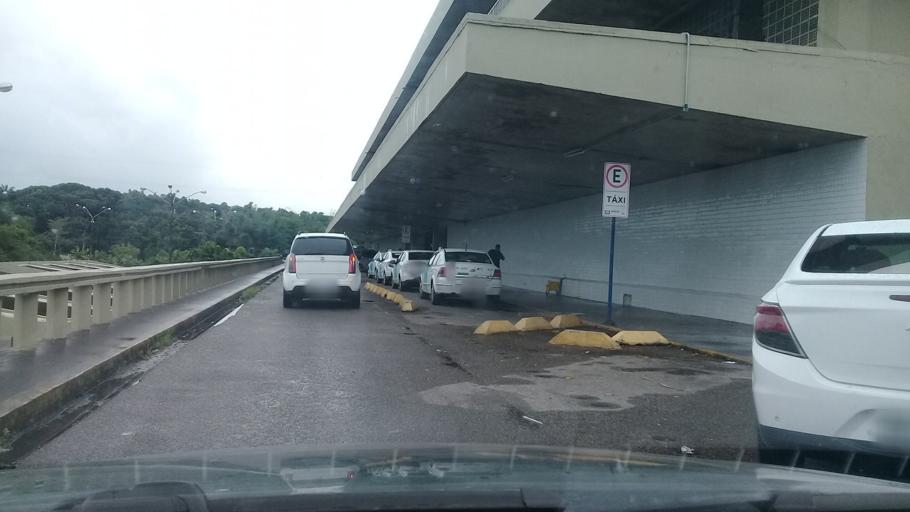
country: BR
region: Pernambuco
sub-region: Jaboatao Dos Guararapes
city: Jaboatao dos Guararapes
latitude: -8.0637
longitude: -34.9827
